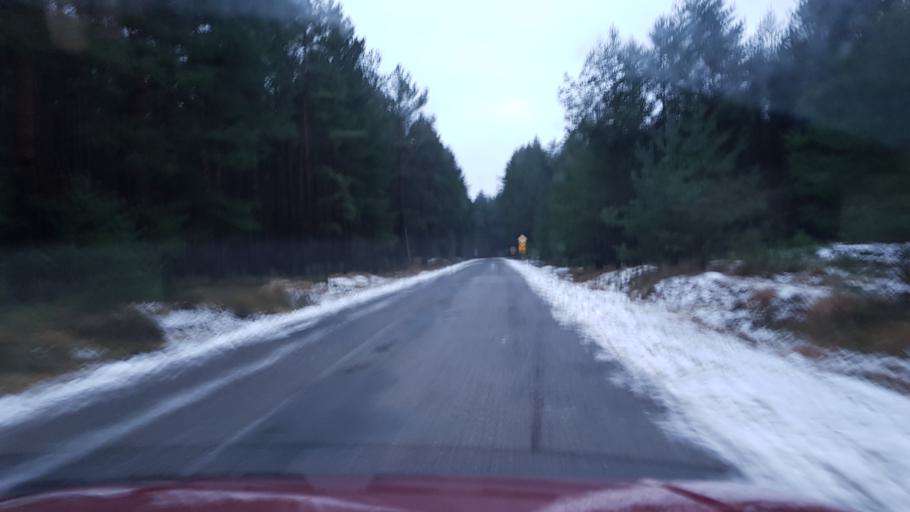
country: PL
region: West Pomeranian Voivodeship
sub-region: Powiat goleniowski
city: Goleniow
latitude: 53.4689
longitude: 14.8311
